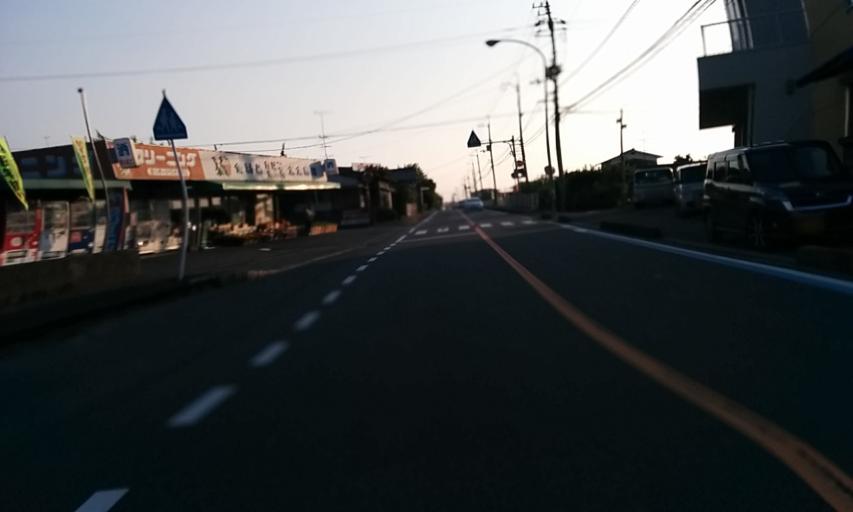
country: JP
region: Ehime
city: Masaki-cho
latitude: 33.7781
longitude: 132.7555
